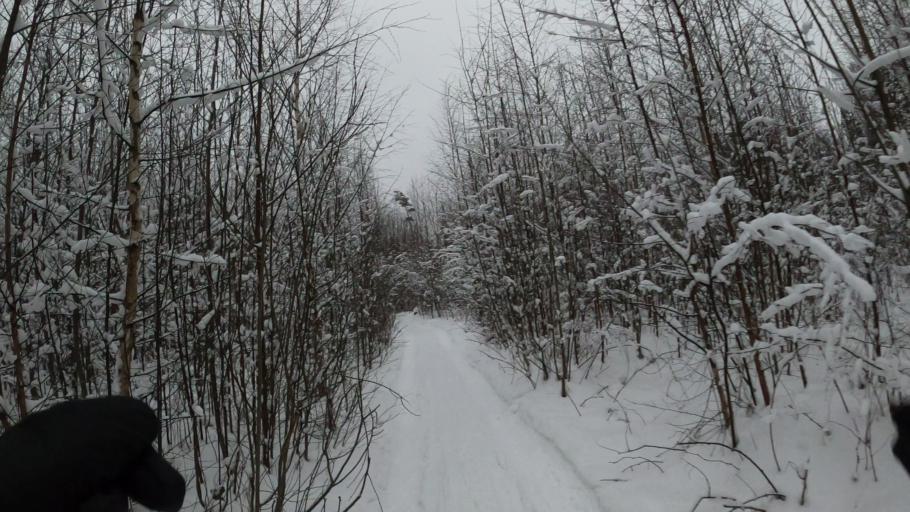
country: RU
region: Moskovskaya
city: Firsanovka
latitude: 55.9095
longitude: 37.2024
